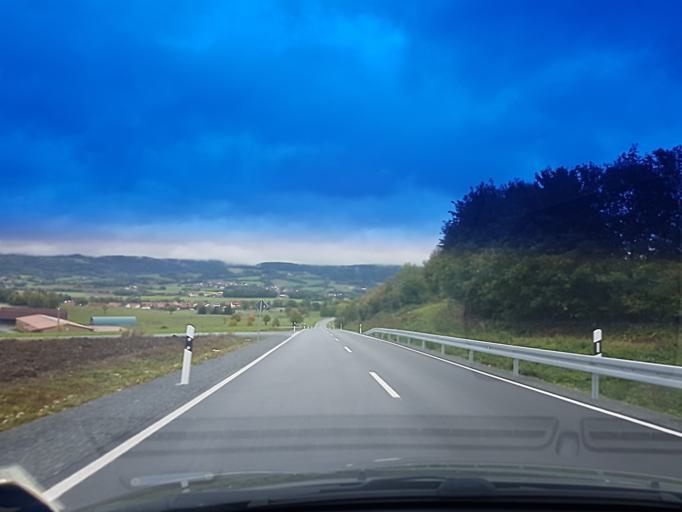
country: DE
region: Bavaria
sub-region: Upper Franconia
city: Bindlach
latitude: 49.9893
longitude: 11.6483
